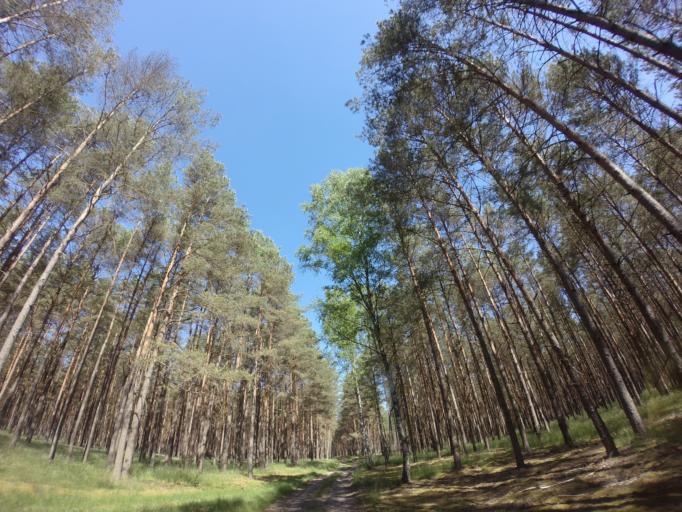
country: PL
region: West Pomeranian Voivodeship
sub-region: Powiat drawski
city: Kalisz Pomorski
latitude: 53.1845
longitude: 15.9817
